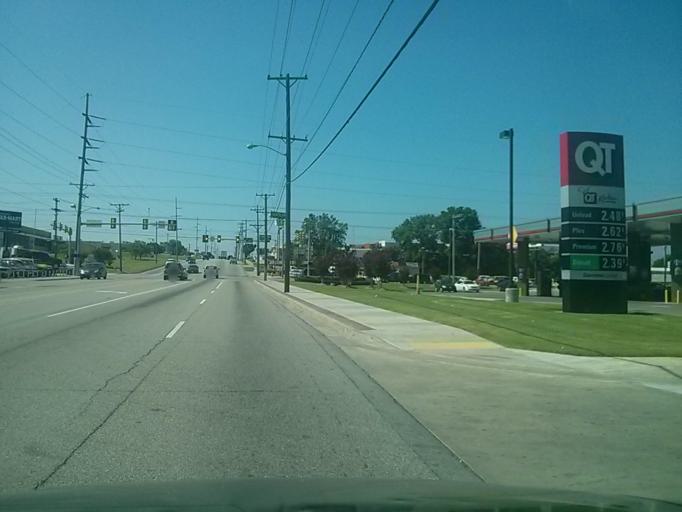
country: US
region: Oklahoma
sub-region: Tulsa County
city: Tulsa
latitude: 36.1488
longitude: -95.9046
